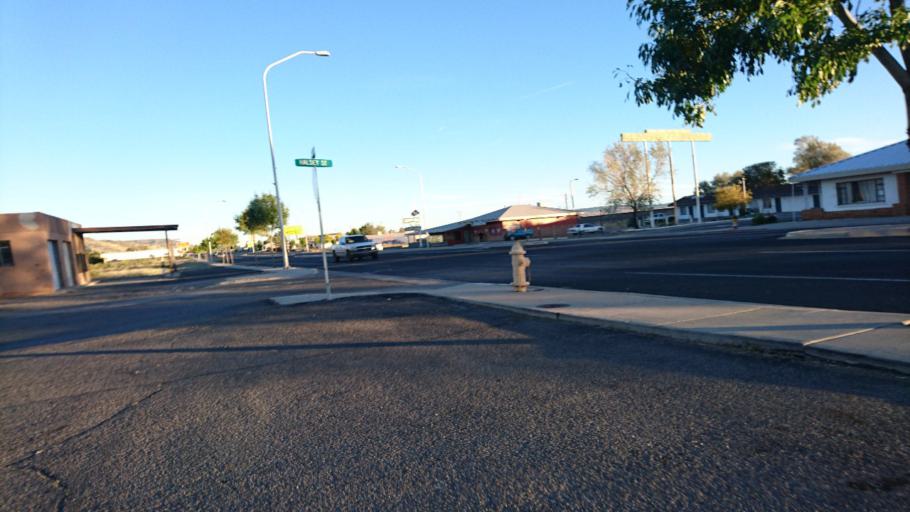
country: US
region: New Mexico
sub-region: Cibola County
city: Grants
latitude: 35.1443
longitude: -107.8372
